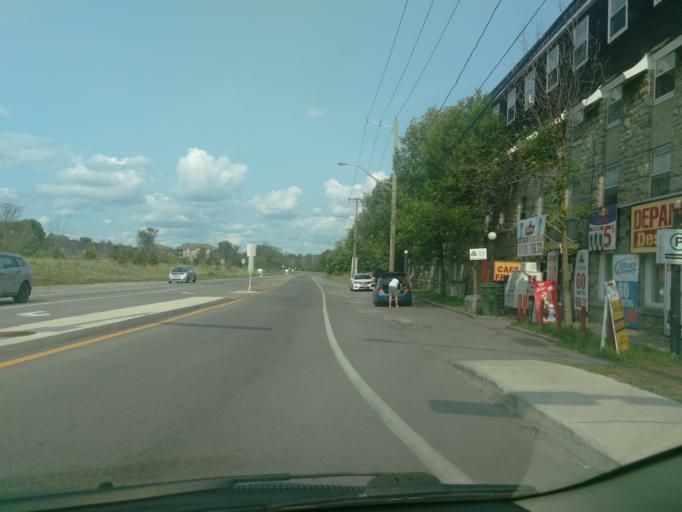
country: CA
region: Ontario
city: Bells Corners
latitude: 45.3866
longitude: -75.8050
